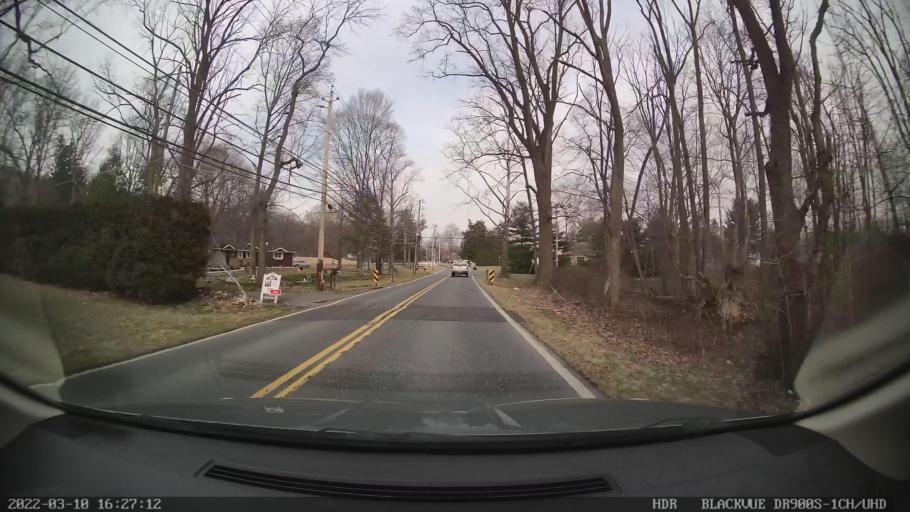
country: US
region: Pennsylvania
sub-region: Berks County
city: Jacksonwald
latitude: 40.3281
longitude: -75.8439
